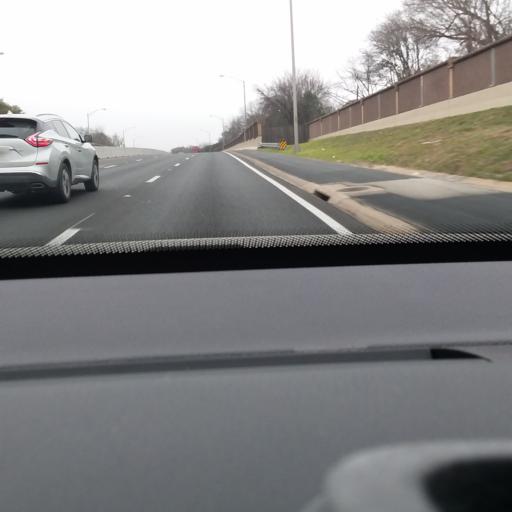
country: US
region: Texas
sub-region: Dallas County
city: University Park
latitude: 32.8527
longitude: -96.7897
